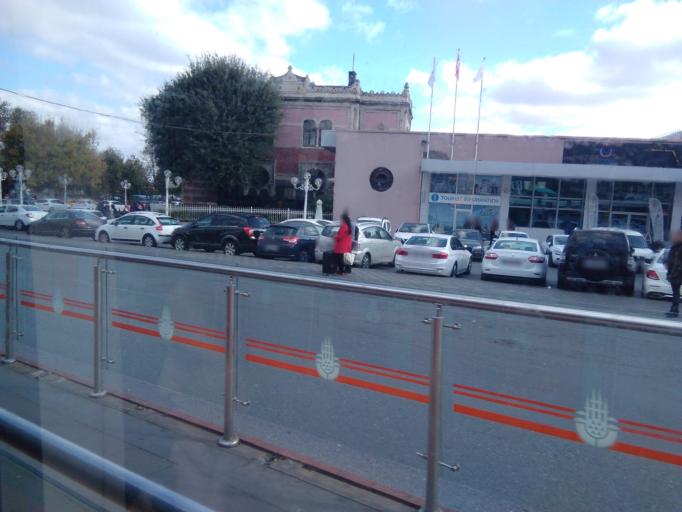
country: TR
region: Istanbul
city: Eminoenue
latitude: 41.0152
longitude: 28.9761
